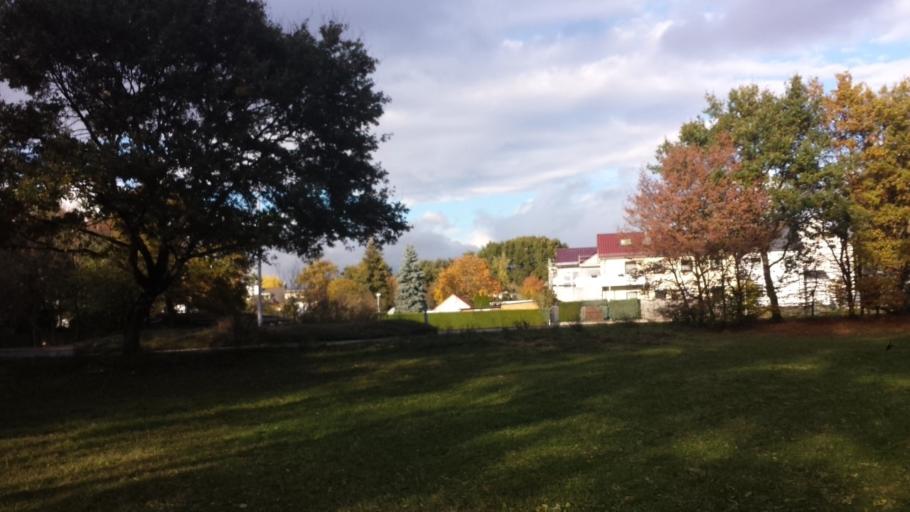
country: DE
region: Hesse
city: Niederrad
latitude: 50.0799
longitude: 8.5979
